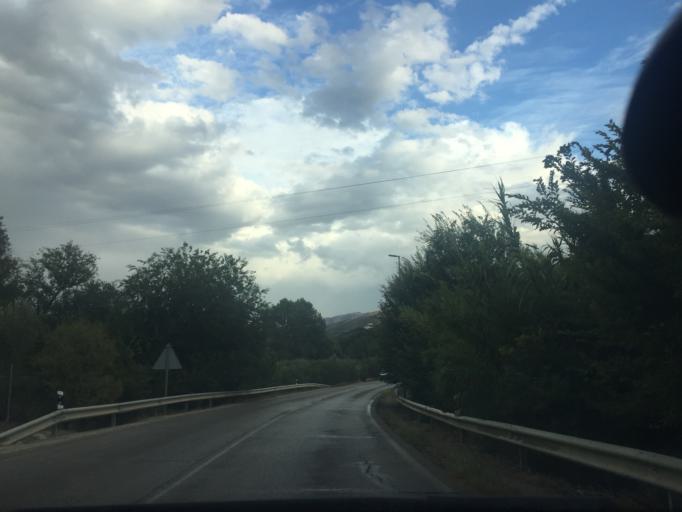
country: ES
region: Andalusia
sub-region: Provincia de Jaen
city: Jaen
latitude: 37.7615
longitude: -3.7583
